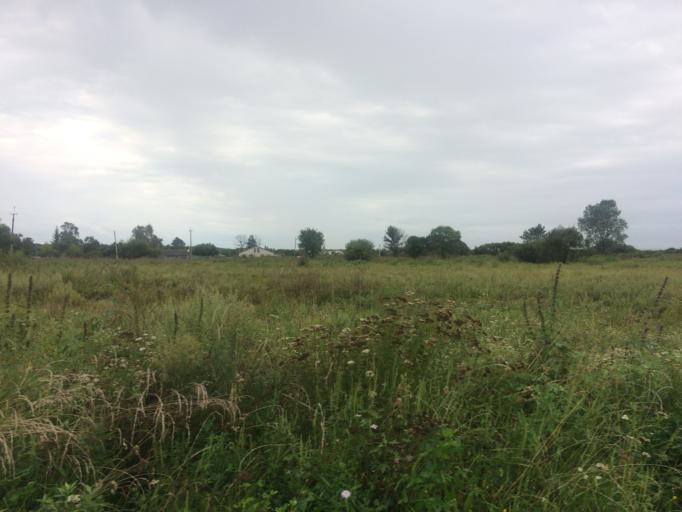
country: RU
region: Primorskiy
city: Lazo
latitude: 45.8305
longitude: 133.6129
